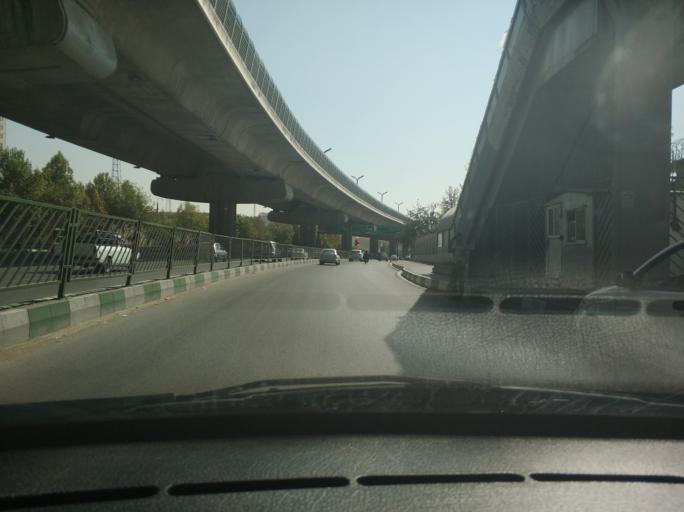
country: IR
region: Tehran
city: Tajrish
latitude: 35.7903
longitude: 51.4796
